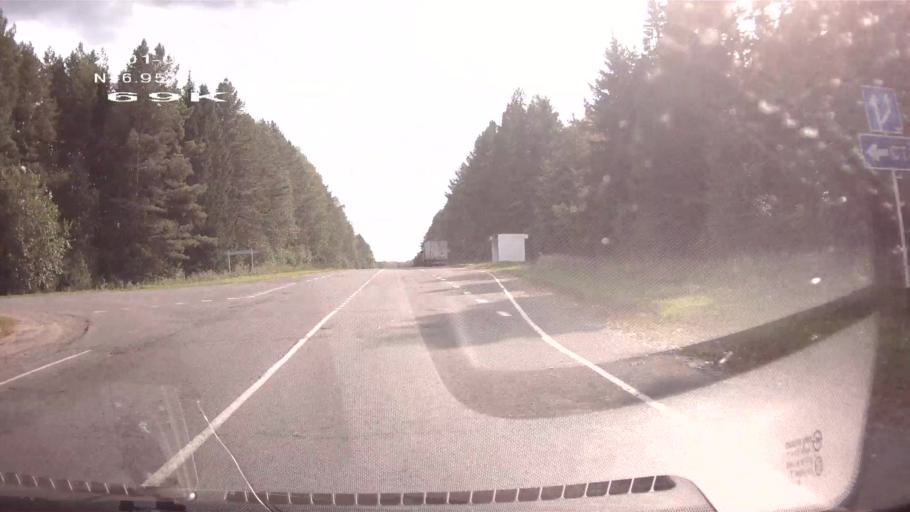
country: RU
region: Mariy-El
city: Kuzhener
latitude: 56.9511
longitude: 48.7504
